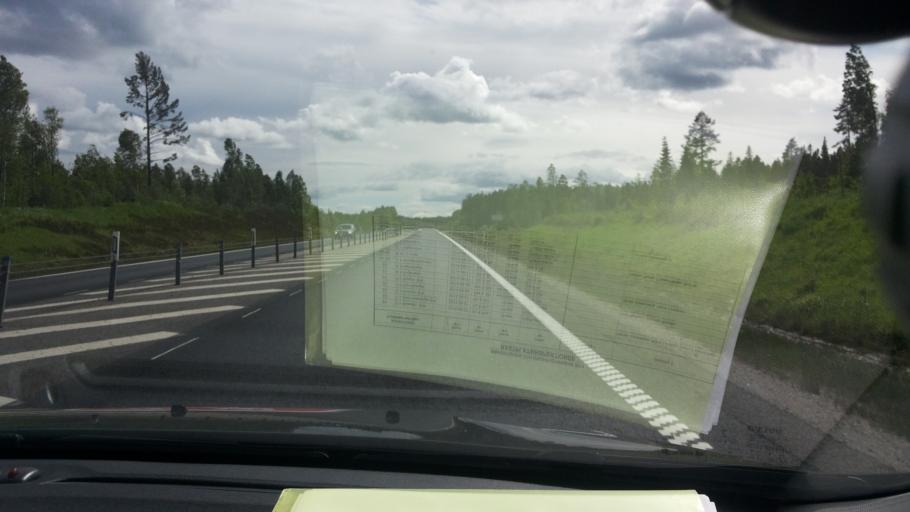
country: SE
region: Vaesternorrland
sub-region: Sundsvalls Kommun
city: Njurundabommen
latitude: 62.2072
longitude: 17.3732
